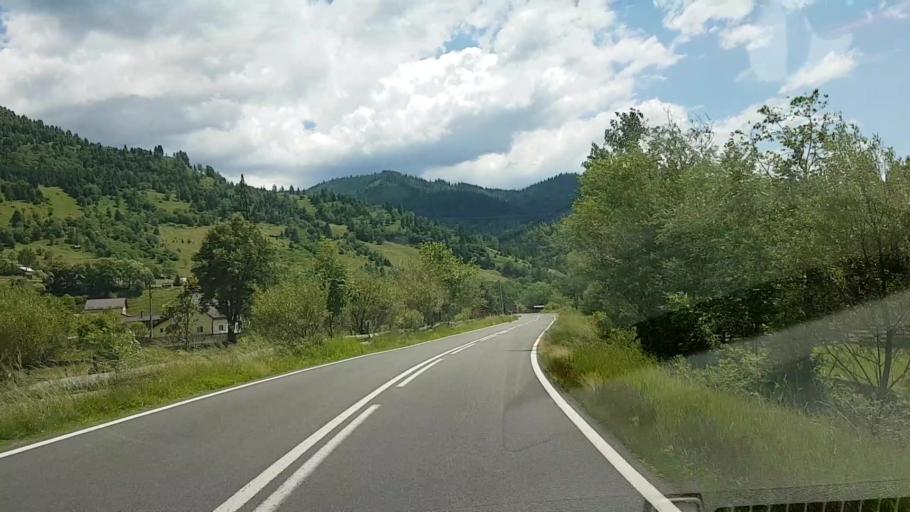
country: RO
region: Suceava
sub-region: Comuna Crucea
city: Crucea
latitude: 47.3931
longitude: 25.5719
